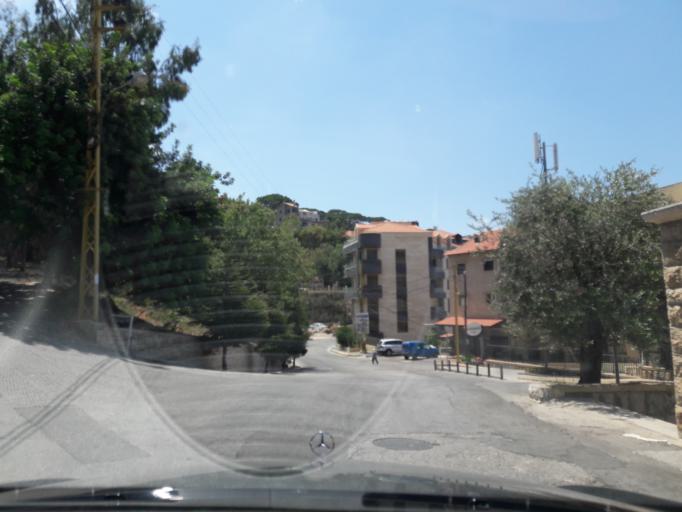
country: LB
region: Mont-Liban
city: Djounie
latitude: 33.9231
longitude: 35.6443
